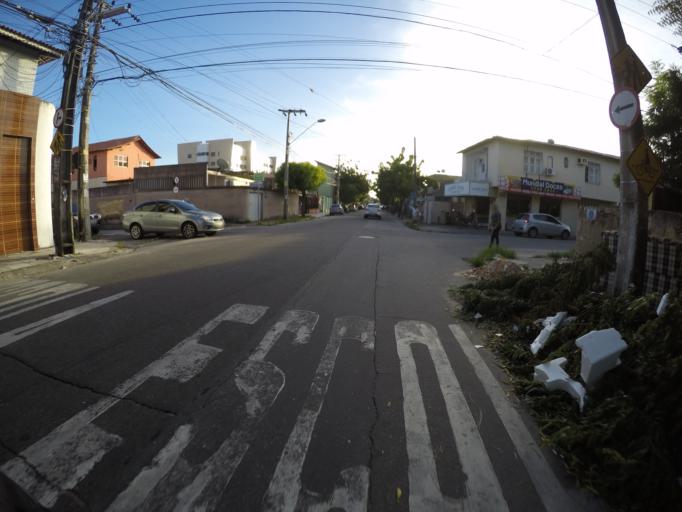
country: BR
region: Ceara
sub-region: Fortaleza
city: Fortaleza
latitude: -3.7561
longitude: -38.5142
